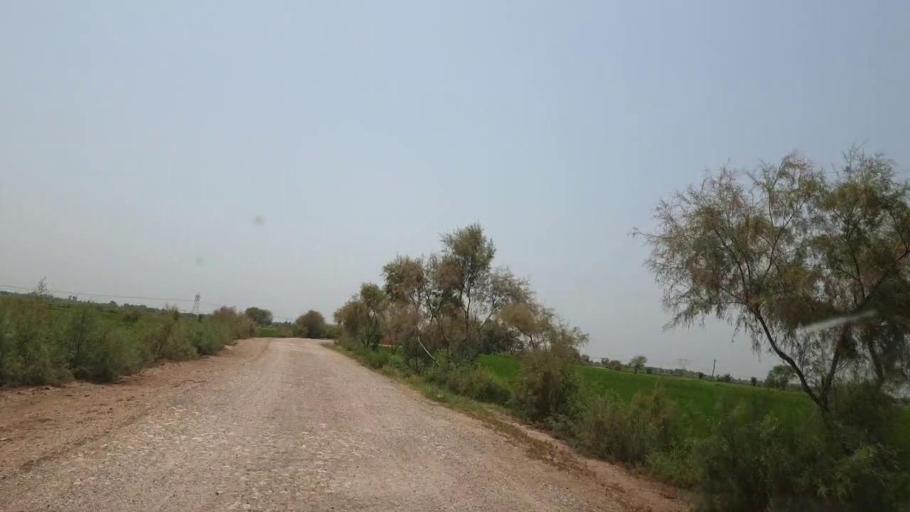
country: PK
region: Sindh
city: Shikarpur
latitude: 27.8988
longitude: 68.6319
